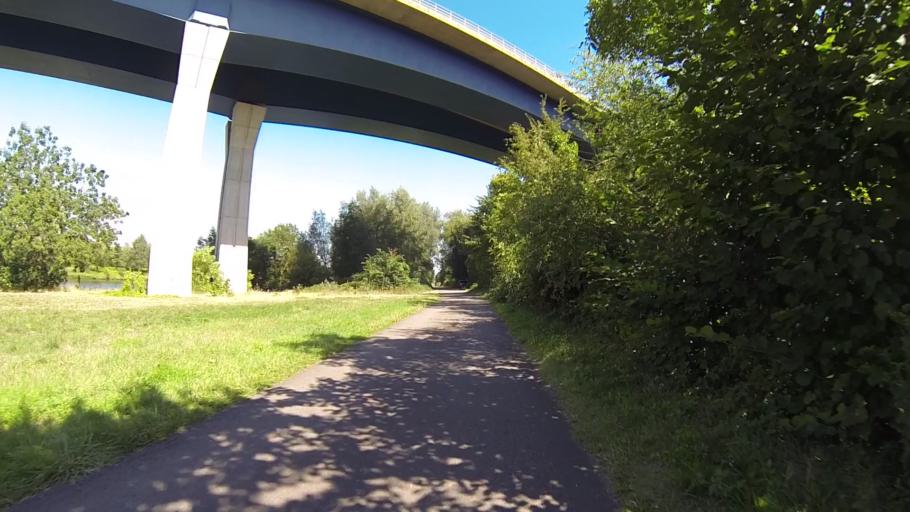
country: LU
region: Grevenmacher
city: Schengen
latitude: 49.4792
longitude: 6.3689
